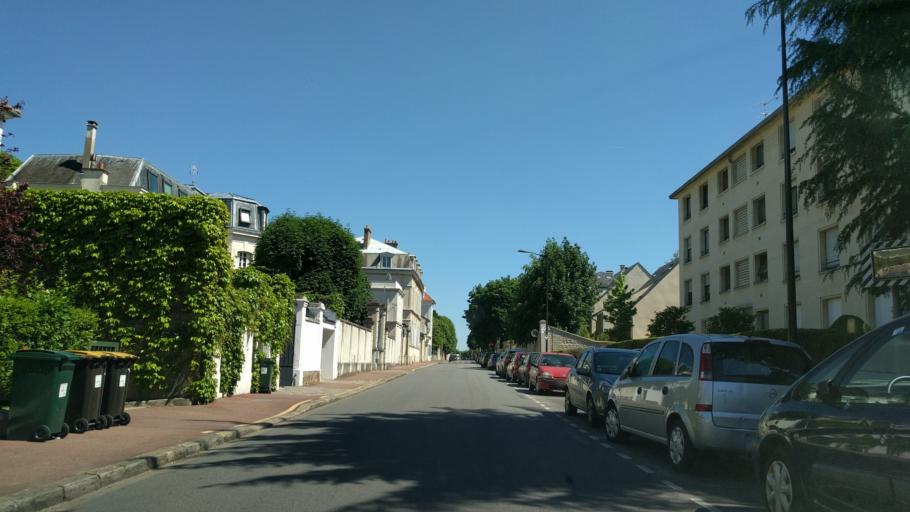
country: FR
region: Ile-de-France
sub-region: Departement des Yvelines
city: Saint-Germain-en-Laye
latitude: 48.9029
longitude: 2.0866
